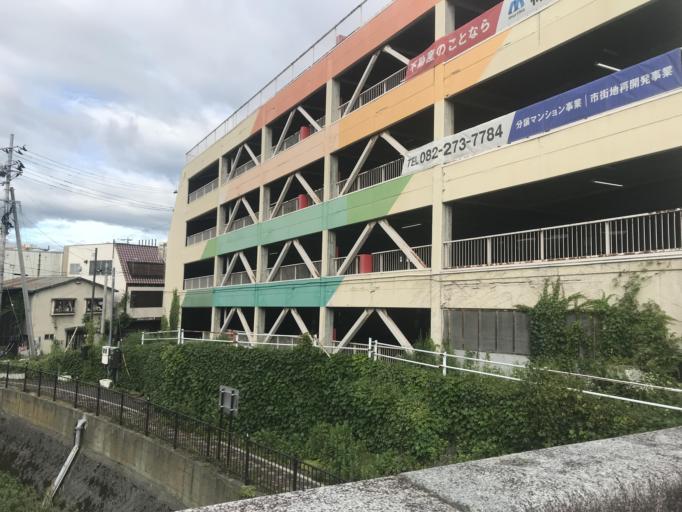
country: JP
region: Aomori
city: Hirosaki
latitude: 40.6012
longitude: 140.4733
